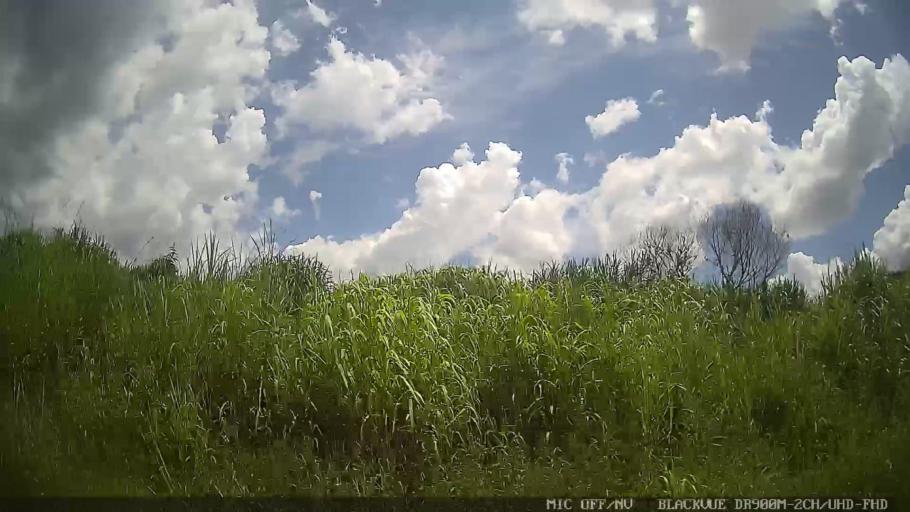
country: BR
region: Sao Paulo
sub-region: Atibaia
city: Atibaia
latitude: -23.1005
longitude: -46.6309
